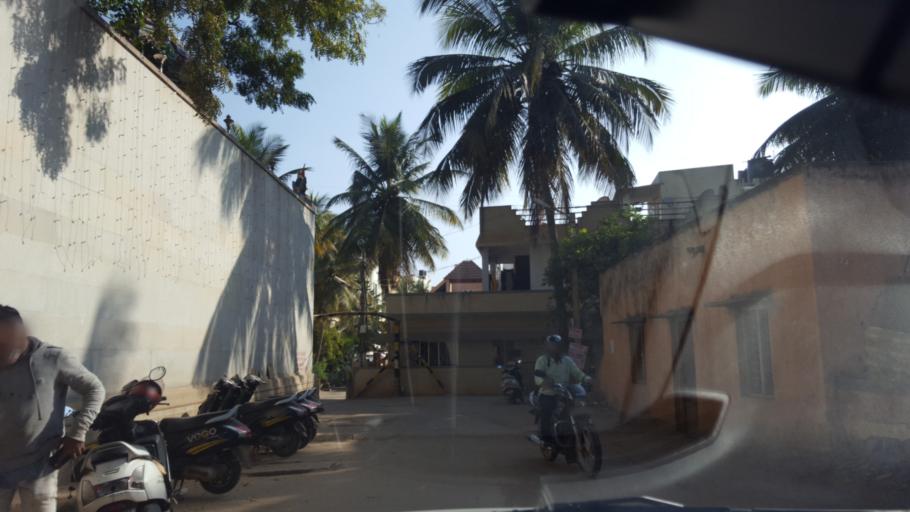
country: IN
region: Karnataka
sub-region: Bangalore Urban
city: Bangalore
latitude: 12.9480
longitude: 77.7083
